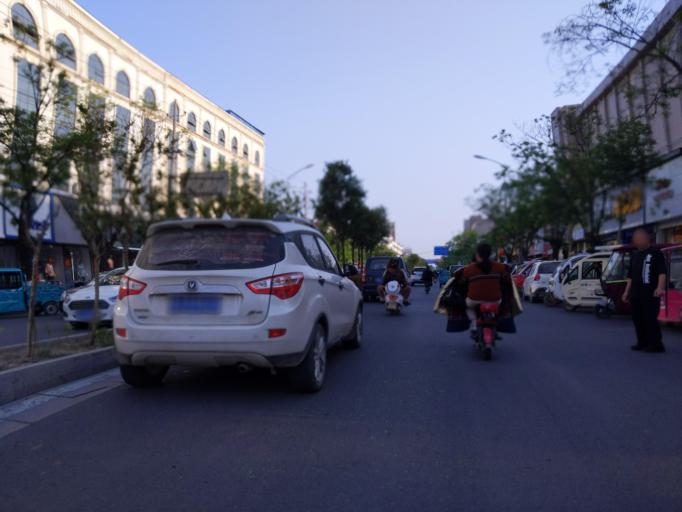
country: CN
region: Henan Sheng
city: Puyang Chengguanzhen
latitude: 35.7036
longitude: 115.0164
